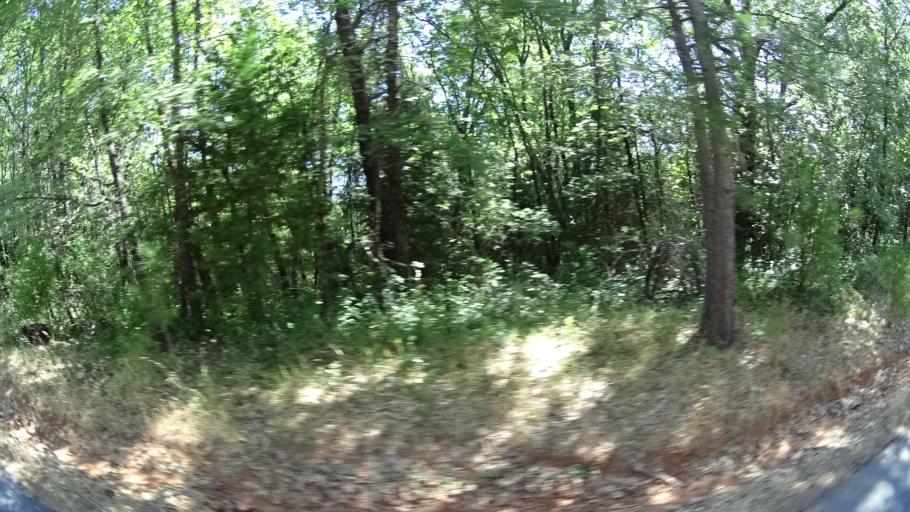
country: US
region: California
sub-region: Amador County
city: Pioneer
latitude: 38.3948
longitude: -120.5043
